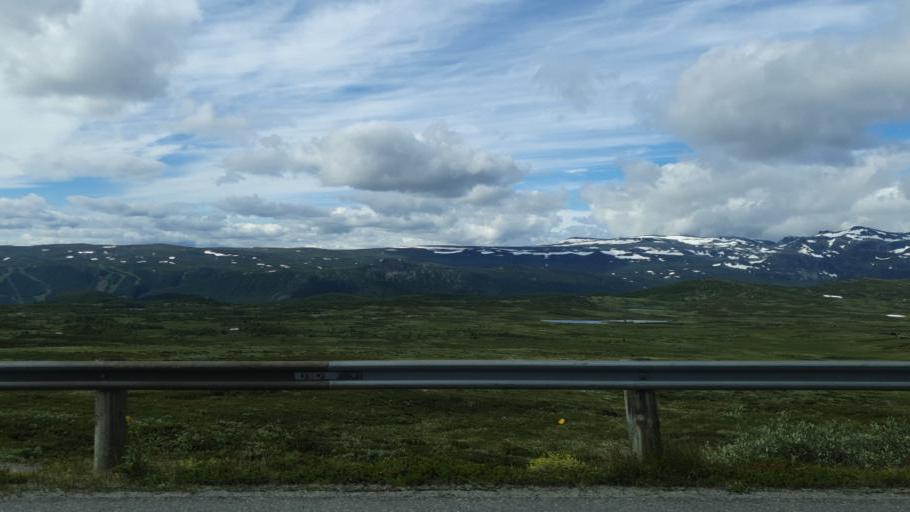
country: NO
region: Oppland
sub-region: Vestre Slidre
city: Slidre
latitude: 61.2772
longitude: 8.8527
